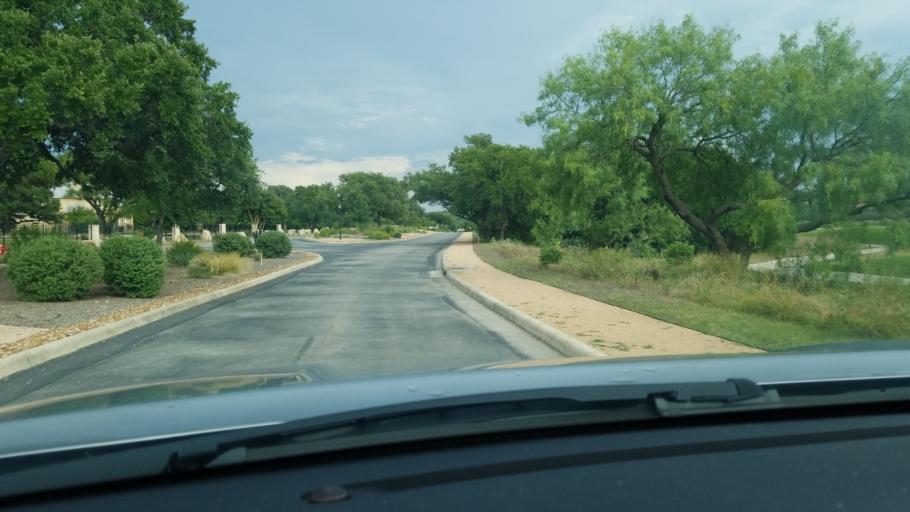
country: US
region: Texas
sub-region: Comal County
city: Bulverde
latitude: 29.8494
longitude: -98.4055
